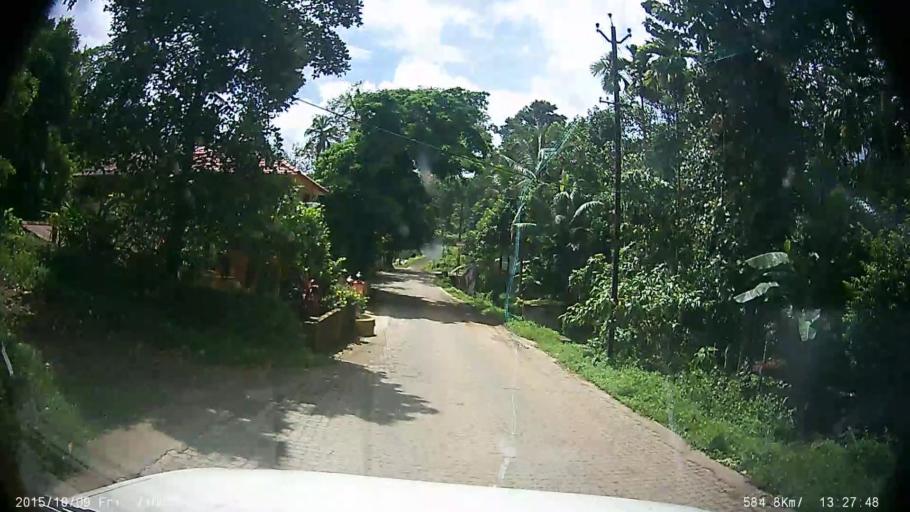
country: IN
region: Kerala
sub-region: Ernakulam
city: Ramamangalam
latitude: 9.9202
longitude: 76.5578
